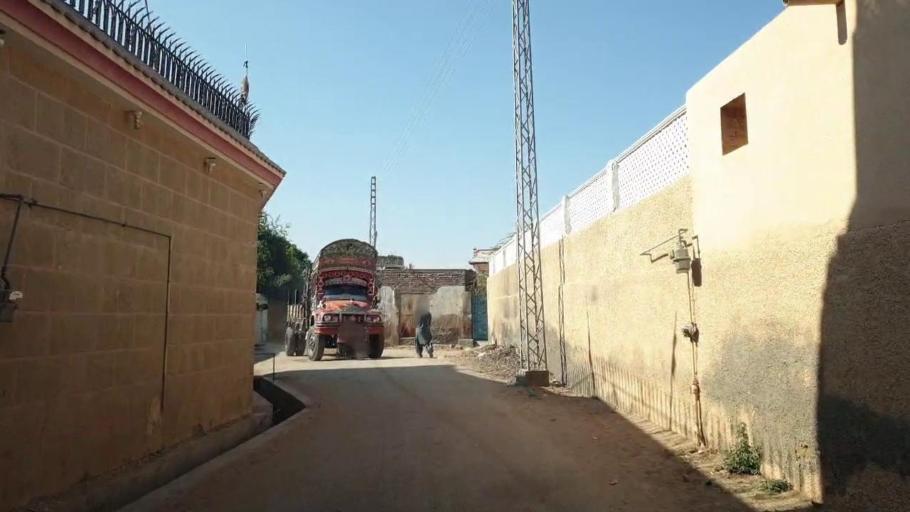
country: PK
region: Sindh
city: Jamshoro
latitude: 25.4104
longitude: 67.7845
